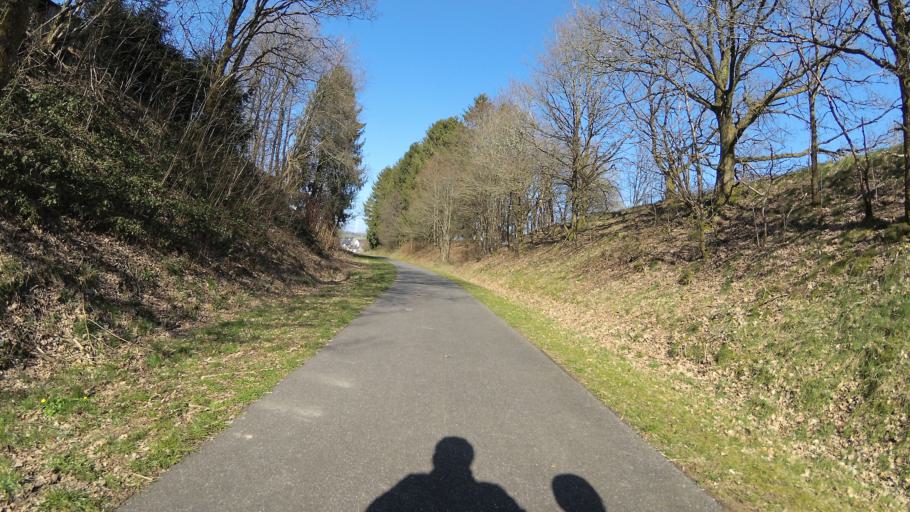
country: DE
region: Rheinland-Pfalz
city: Reinsfeld
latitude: 49.6710
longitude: 6.8761
